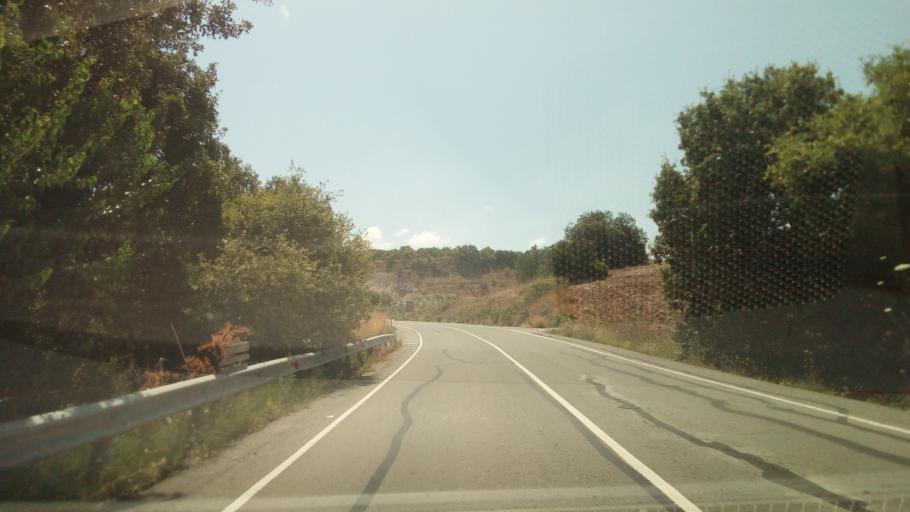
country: CY
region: Pafos
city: Polis
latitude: 34.9502
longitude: 32.4904
